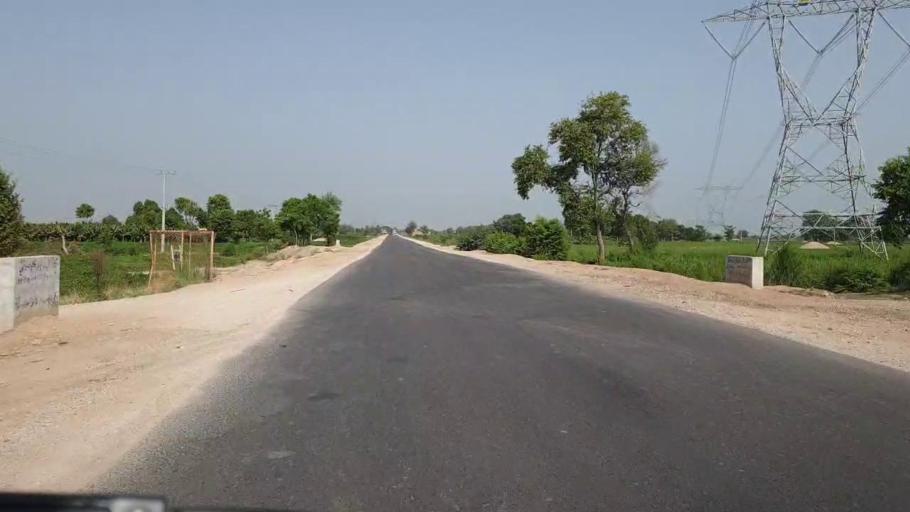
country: PK
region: Sindh
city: Sakrand
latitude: 26.2531
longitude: 68.2025
